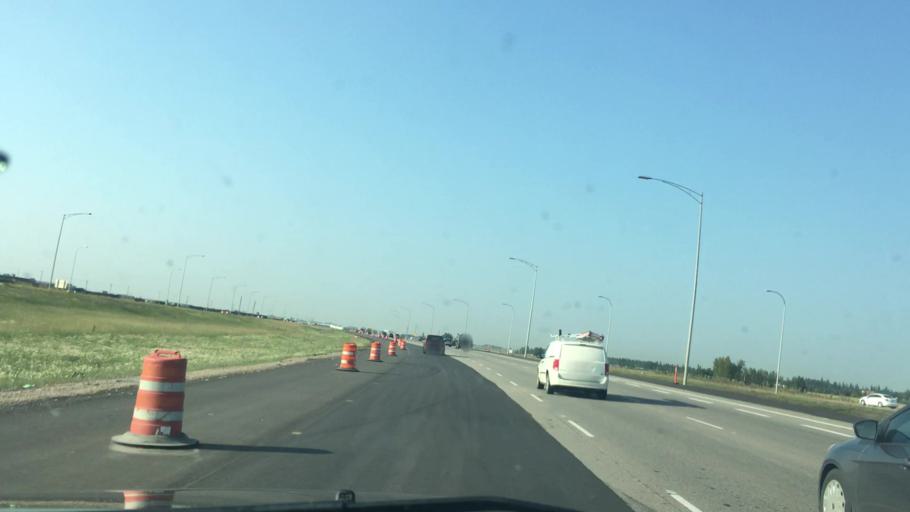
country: CA
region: Alberta
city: Beaumont
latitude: 53.3961
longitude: -113.5129
